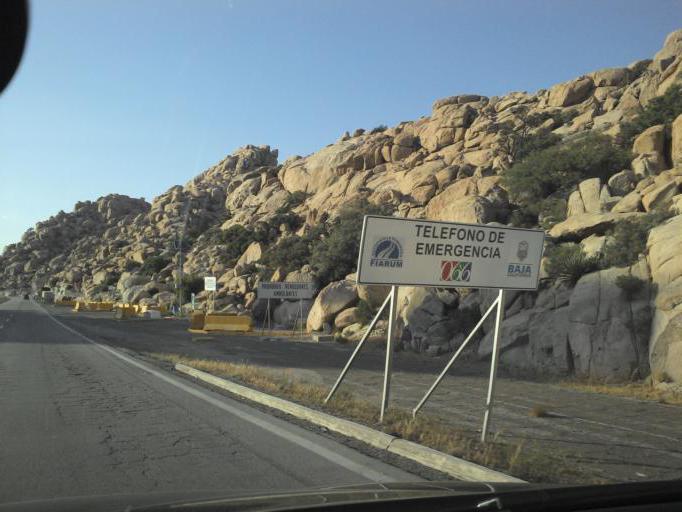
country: MX
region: Baja California
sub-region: Tecate
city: Cereso del Hongo
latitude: 32.5600
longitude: -116.0360
